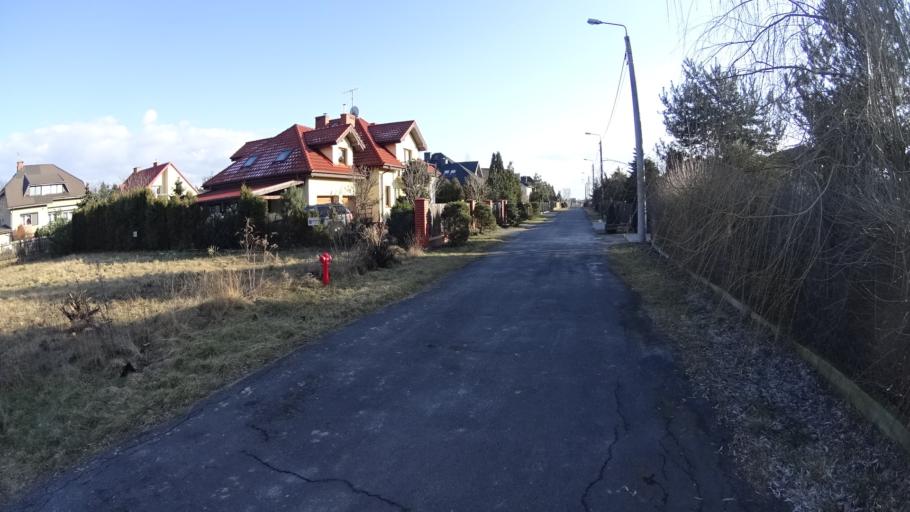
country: PL
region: Masovian Voivodeship
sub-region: Powiat warszawski zachodni
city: Hornowek
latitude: 52.2639
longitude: 20.7898
